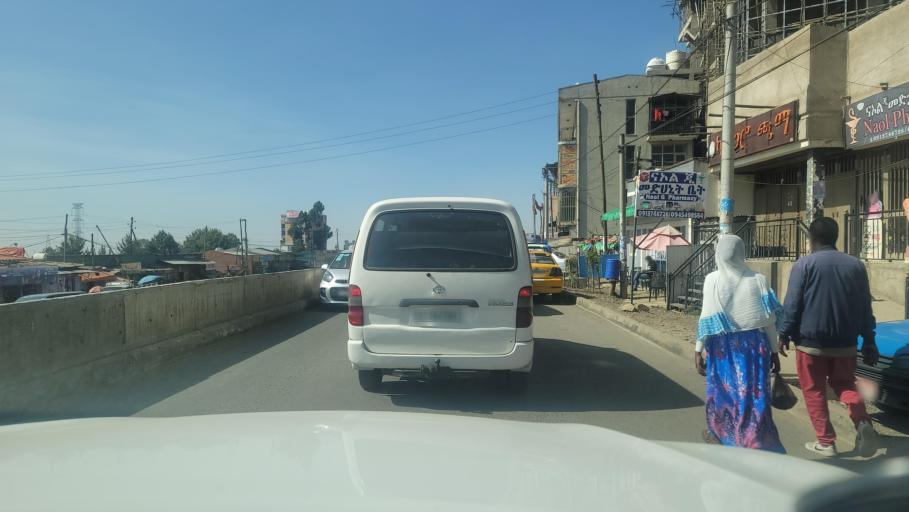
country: ET
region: Adis Abeba
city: Addis Ababa
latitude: 9.0367
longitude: 38.8296
